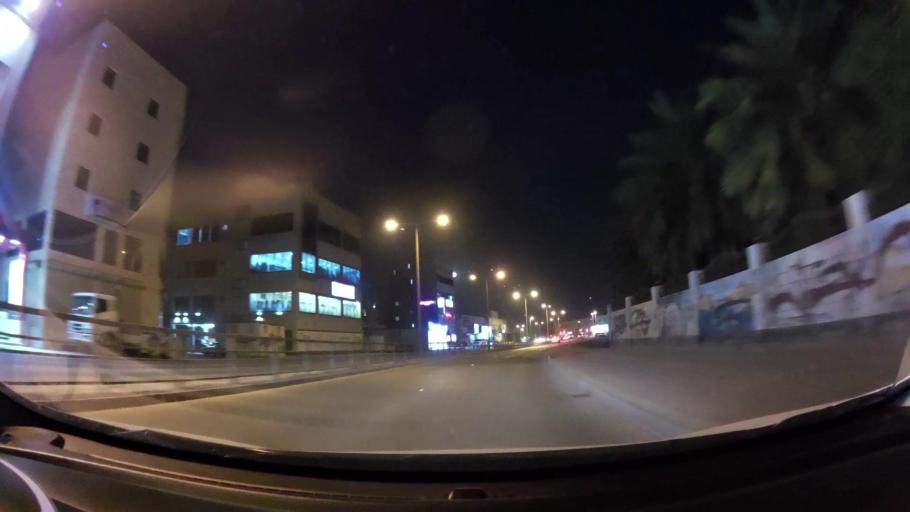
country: BH
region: Manama
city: Jidd Hafs
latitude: 26.2211
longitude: 50.5386
